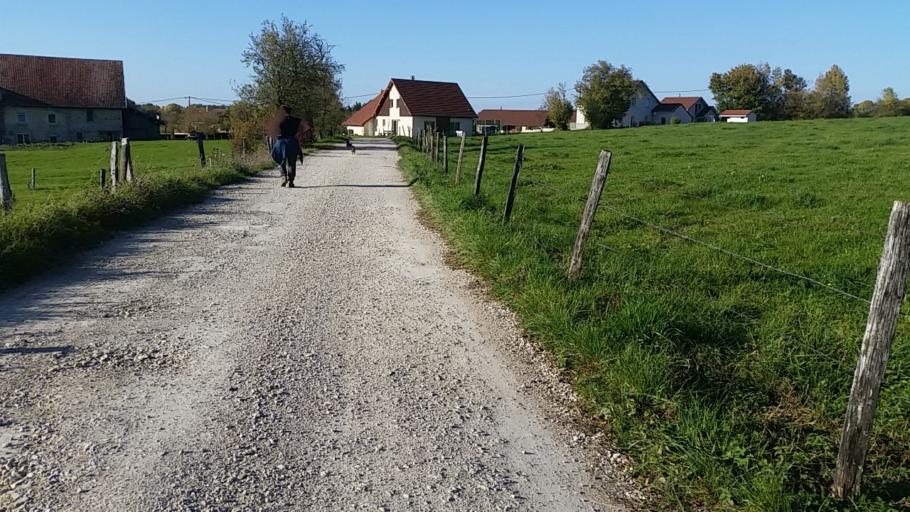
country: FR
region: Franche-Comte
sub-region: Departement du Doubs
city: Ornans
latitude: 47.0521
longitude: 6.0666
